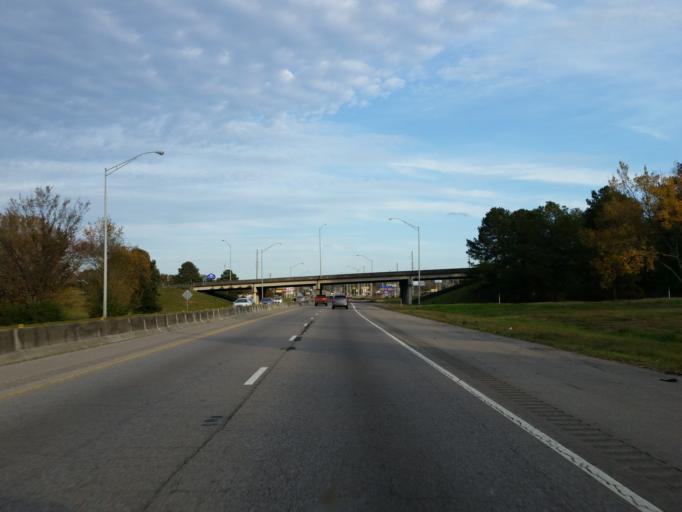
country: US
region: Mississippi
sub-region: Lauderdale County
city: Meridian
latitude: 32.3490
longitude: -88.7130
